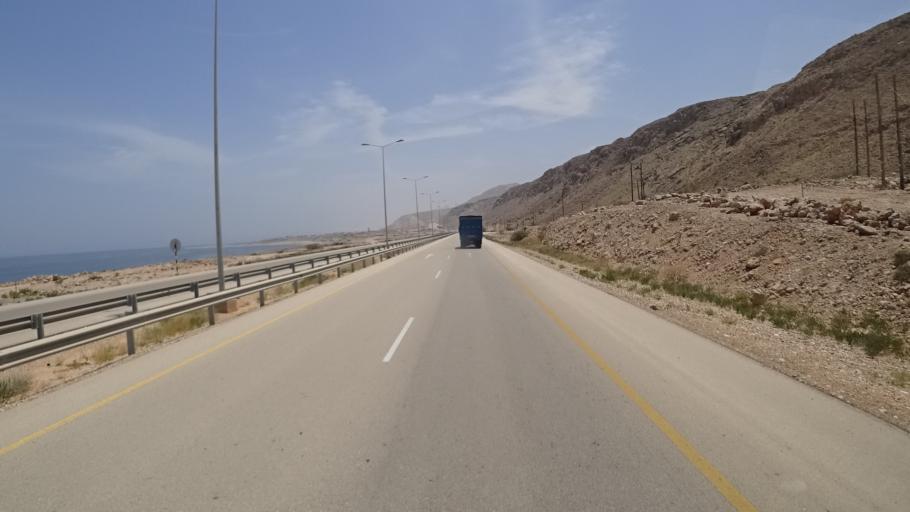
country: OM
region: Ash Sharqiyah
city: Sur
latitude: 22.7189
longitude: 59.3493
